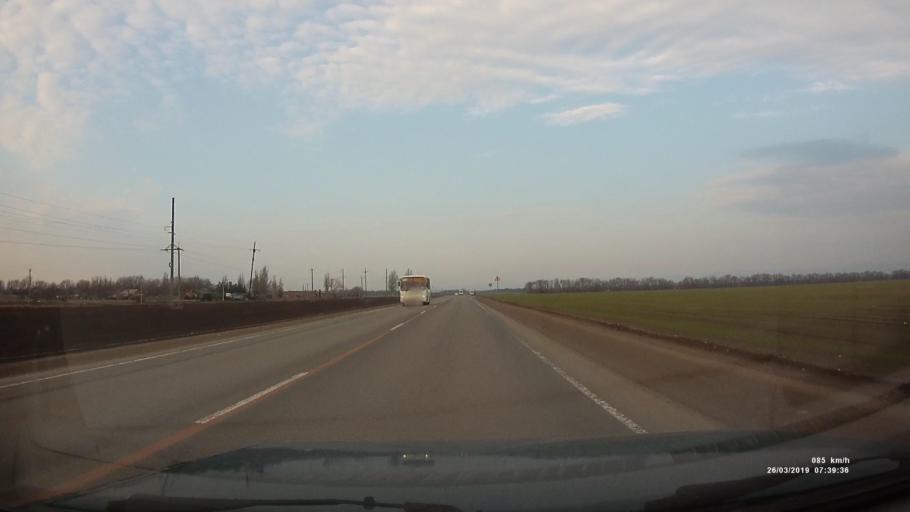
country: RU
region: Rostov
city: Novobessergenovka
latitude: 47.1968
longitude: 38.6623
